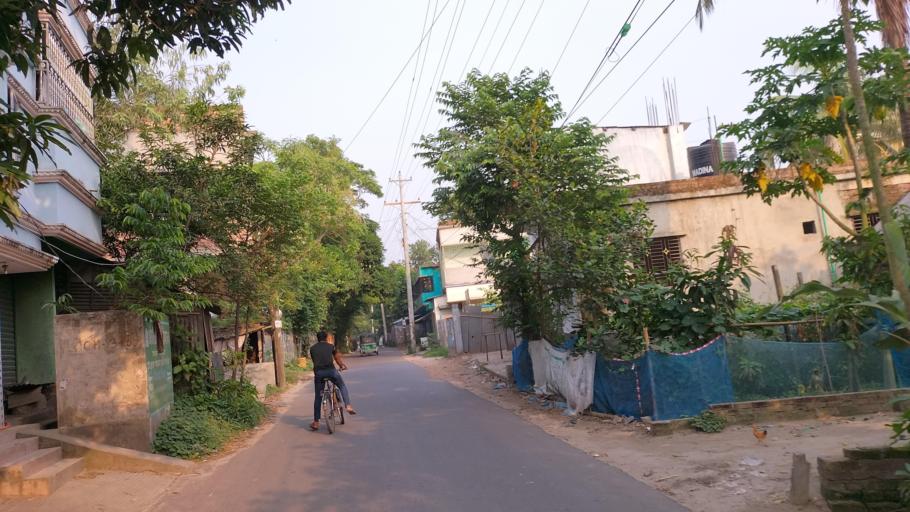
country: BD
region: Dhaka
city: Azimpur
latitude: 23.6664
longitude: 90.3276
